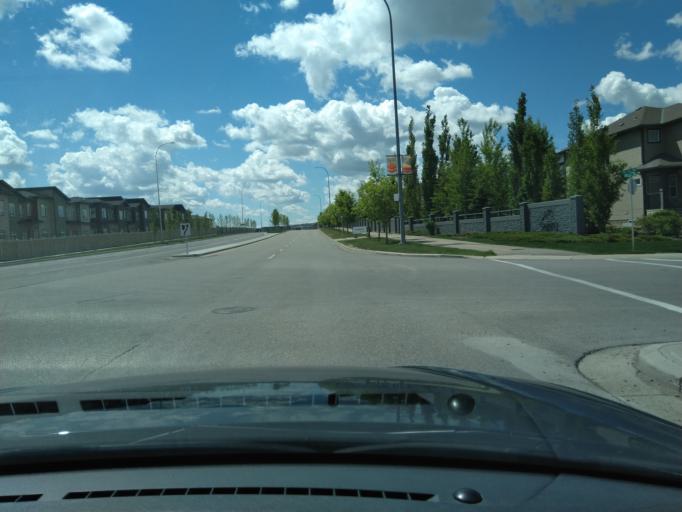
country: CA
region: Alberta
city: Calgary
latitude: 51.1788
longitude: -114.1414
